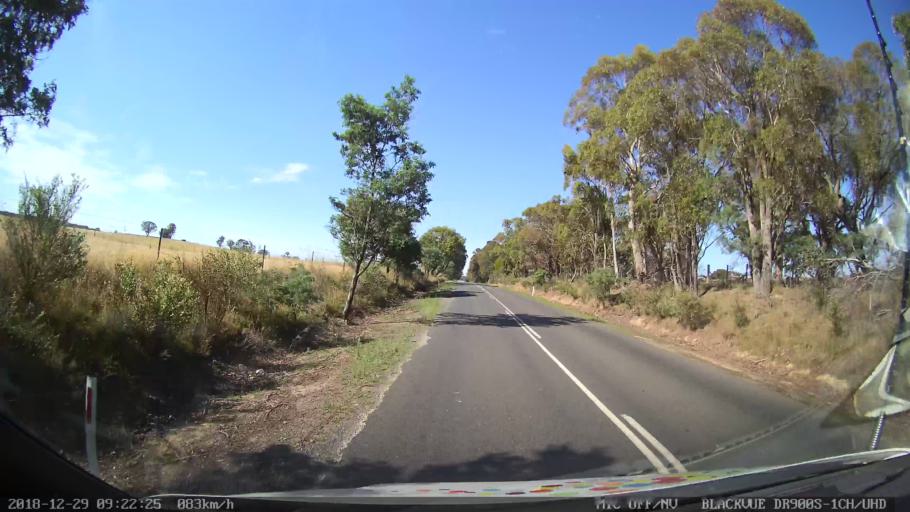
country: AU
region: New South Wales
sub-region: Upper Lachlan Shire
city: Crookwell
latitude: -34.5121
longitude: 149.4060
